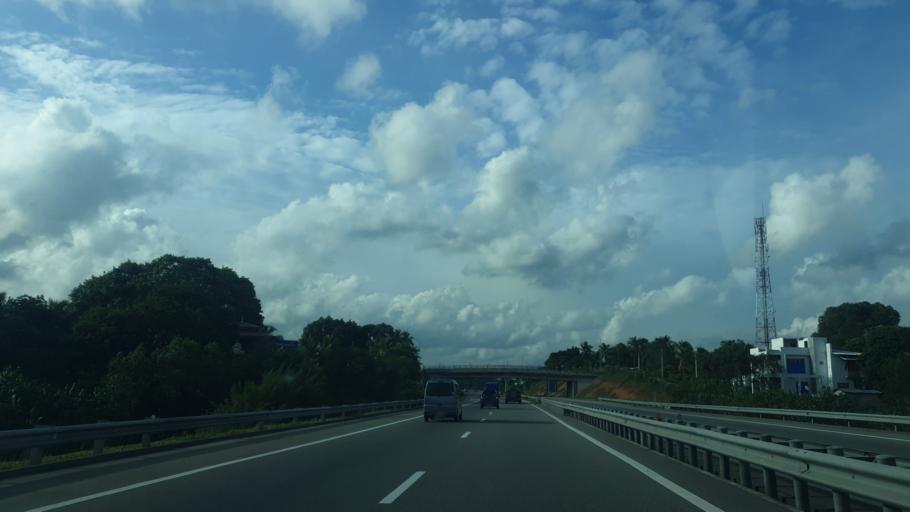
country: LK
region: Western
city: Mulleriyawa
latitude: 6.9484
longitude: 79.9756
